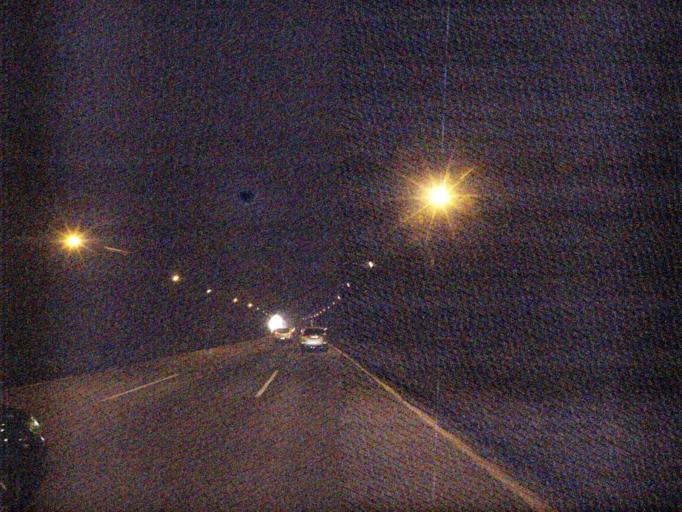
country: BR
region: Rio de Janeiro
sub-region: Rio De Janeiro
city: Rio de Janeiro
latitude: -22.9572
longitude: -43.2051
